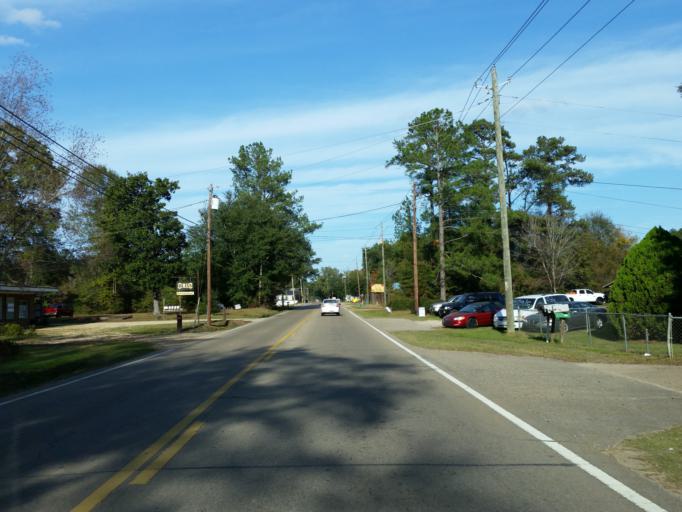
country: US
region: Mississippi
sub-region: Jones County
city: Ellisville
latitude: 31.6475
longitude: -89.1750
